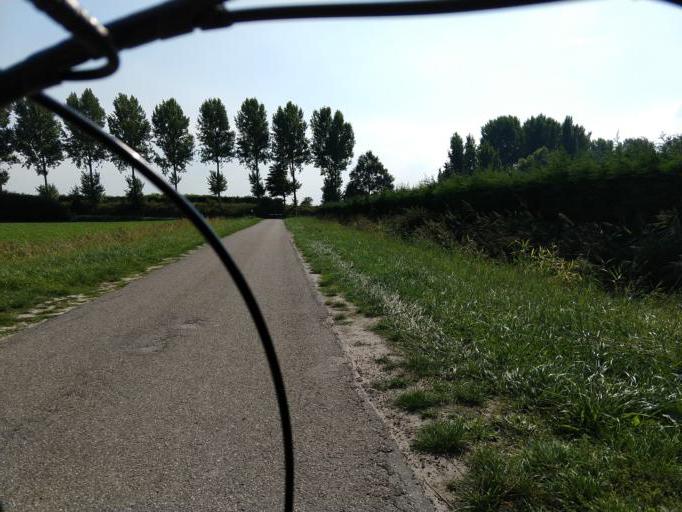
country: NL
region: Zeeland
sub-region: Gemeente Terneuzen
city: Terneuzen
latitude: 51.4061
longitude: 3.8672
